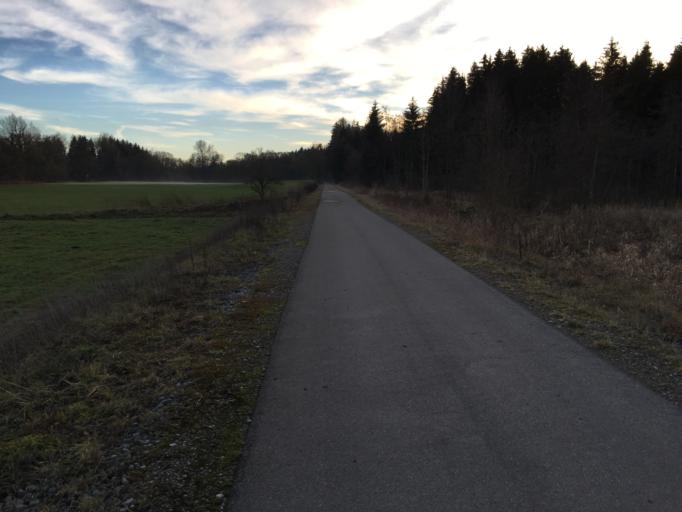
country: DE
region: Bavaria
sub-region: Swabia
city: Westerheim
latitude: 47.9973
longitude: 10.2887
